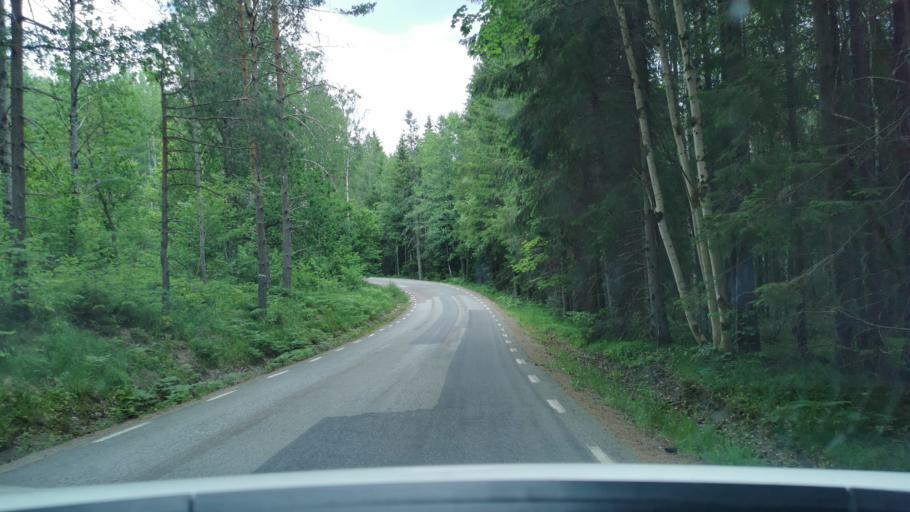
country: SE
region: Vaestra Goetaland
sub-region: Bengtsfors Kommun
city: Dals Langed
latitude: 58.8535
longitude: 12.4048
